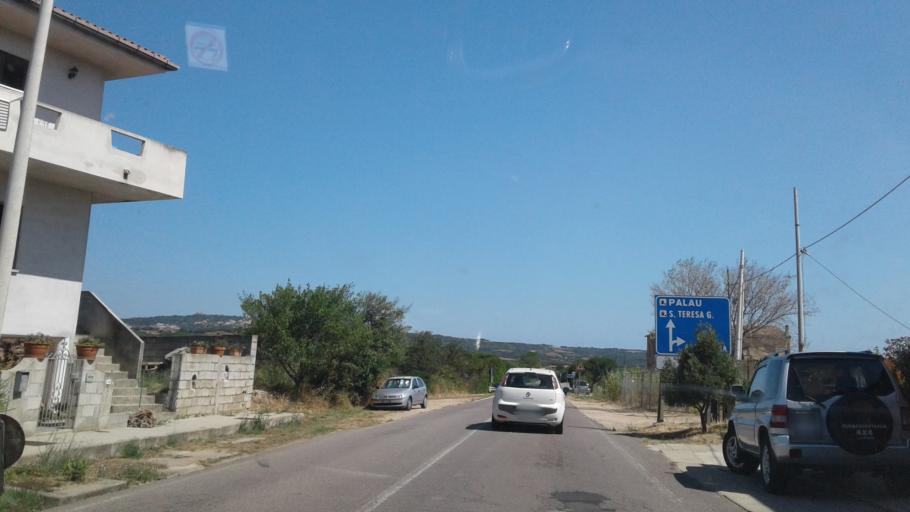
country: IT
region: Sardinia
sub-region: Provincia di Olbia-Tempio
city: Luogosanto
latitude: 41.1104
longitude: 9.2622
